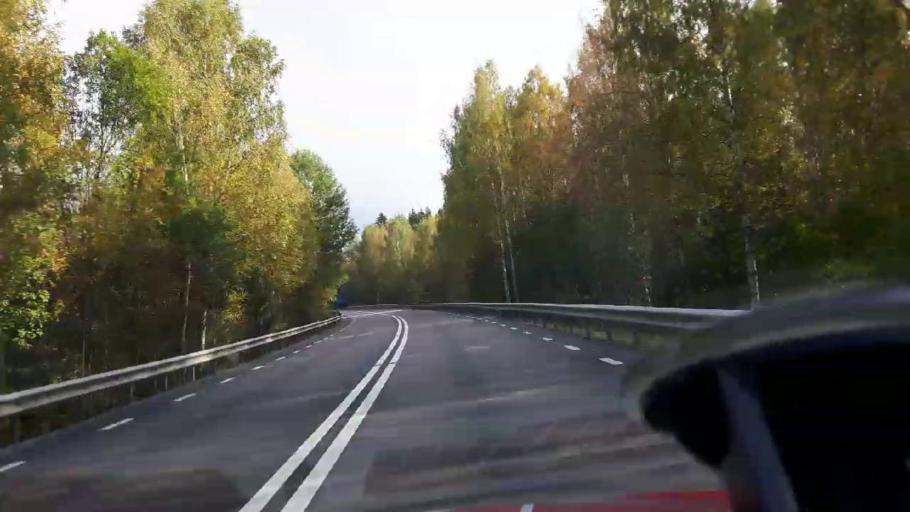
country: SE
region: Gaevleborg
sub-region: Soderhamns Kommun
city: Soderhamn
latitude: 61.1658
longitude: 16.8306
